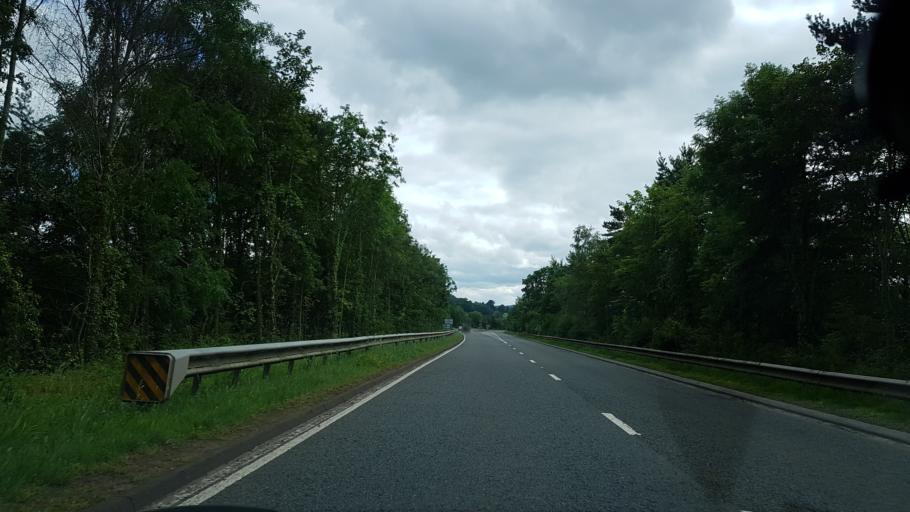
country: GB
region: Wales
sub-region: Monmouthshire
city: Abergavenny
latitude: 51.8380
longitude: -2.9997
